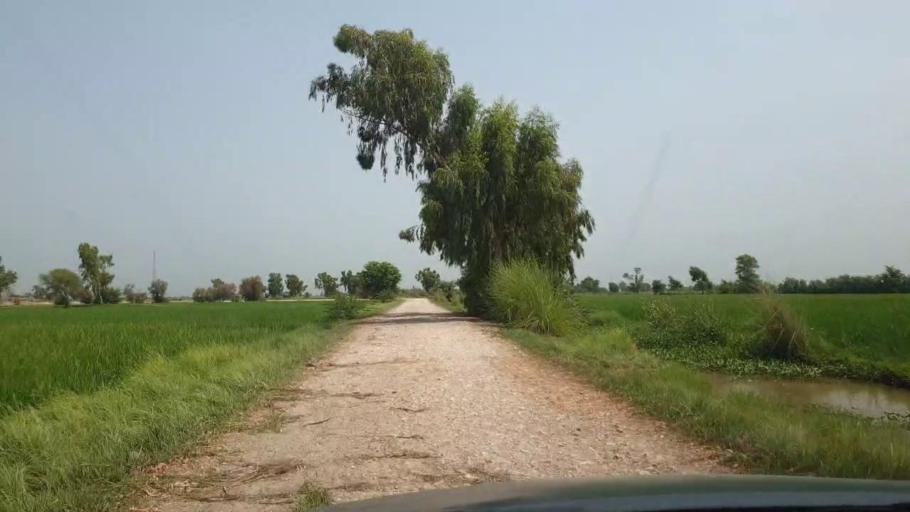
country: PK
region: Sindh
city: Madeji
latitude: 27.7961
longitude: 68.5317
